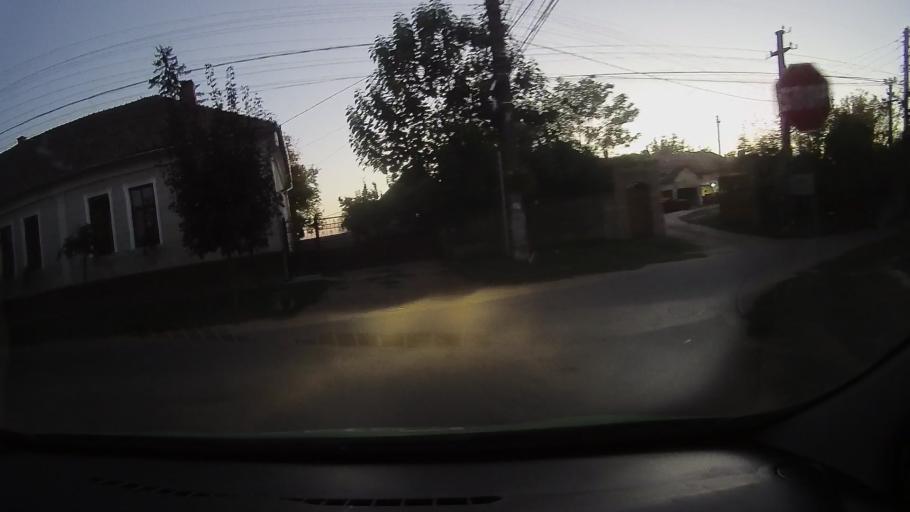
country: RO
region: Bihor
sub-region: Comuna Simian
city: Simian
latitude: 47.4944
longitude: 22.0879
